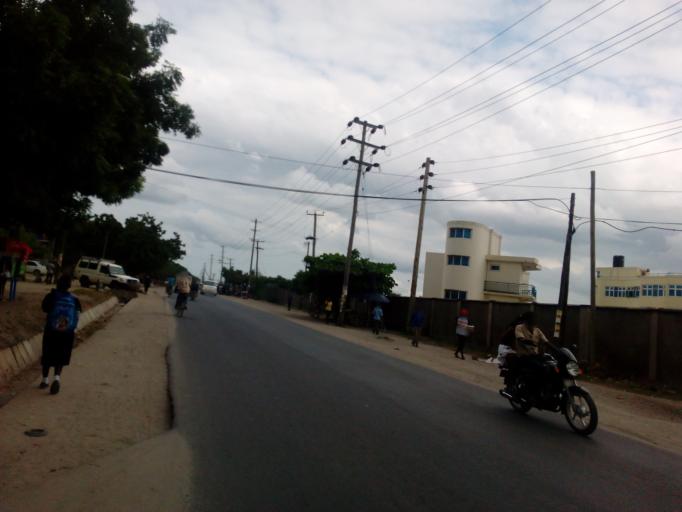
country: TZ
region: Dar es Salaam
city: Dar es Salaam
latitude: -6.8507
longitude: 39.2518
